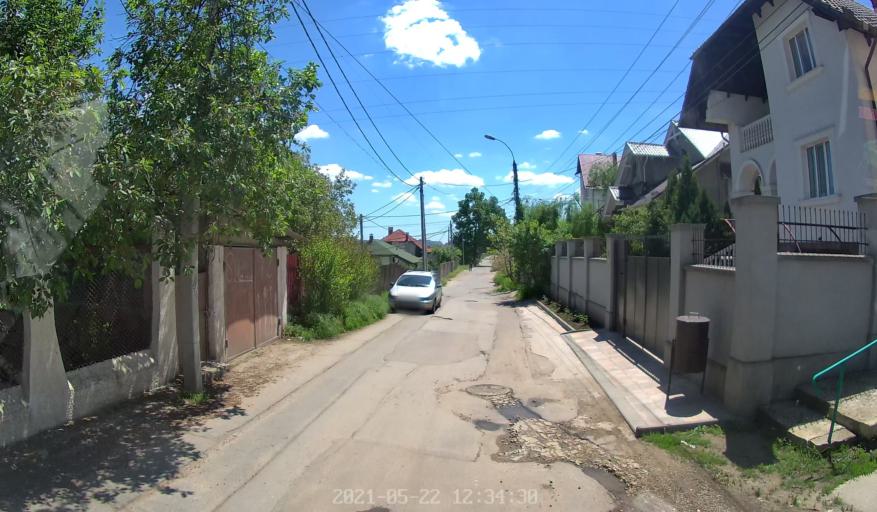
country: MD
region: Chisinau
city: Chisinau
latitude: 47.0493
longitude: 28.8348
